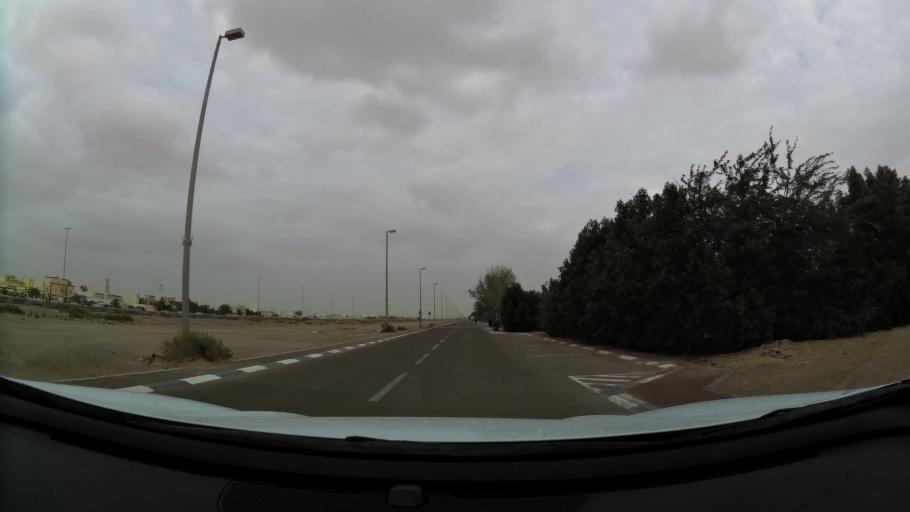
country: AE
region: Abu Dhabi
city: Abu Dhabi
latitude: 24.3441
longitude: 54.6491
